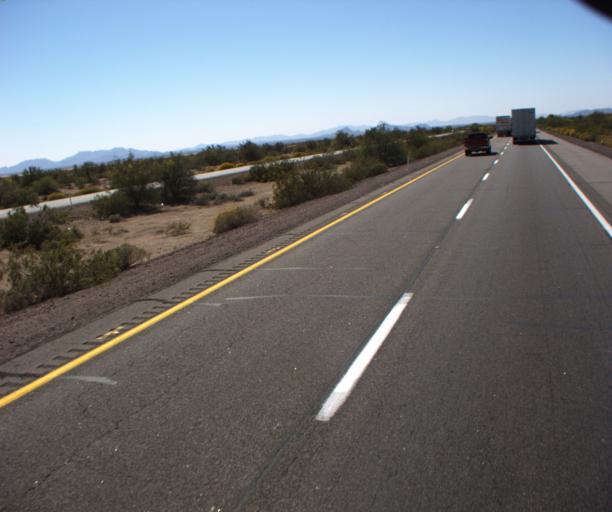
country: US
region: Arizona
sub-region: Yuma County
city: Wellton
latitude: 32.7206
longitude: -113.7760
